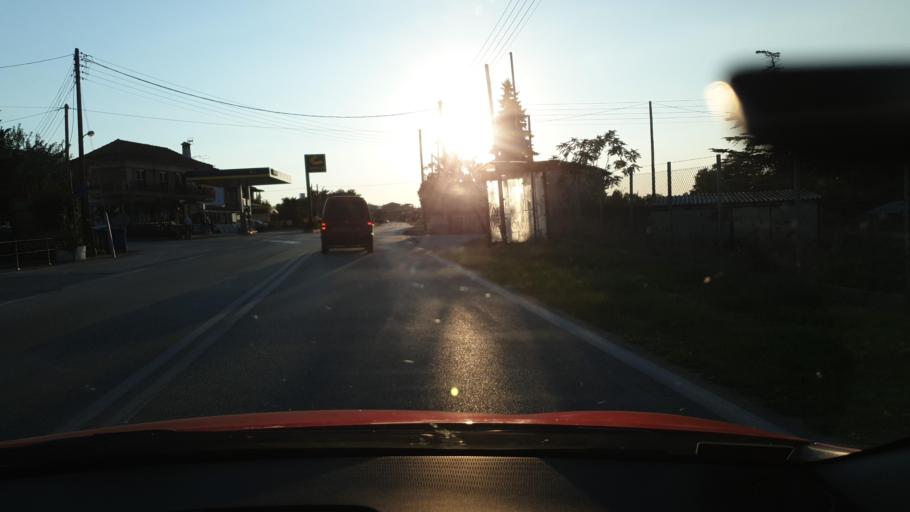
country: GR
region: Central Macedonia
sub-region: Nomos Thessalonikis
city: Nea Apollonia
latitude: 40.5032
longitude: 23.4534
